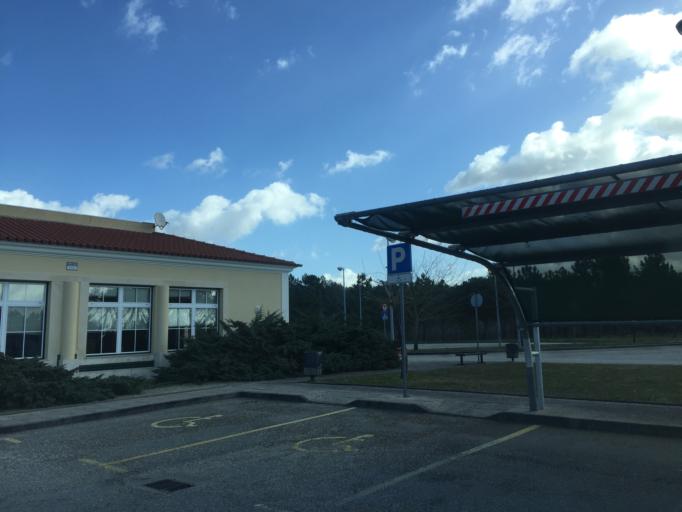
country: PT
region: Leiria
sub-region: Alcobaca
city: Pataias
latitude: 39.6199
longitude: -8.9905
